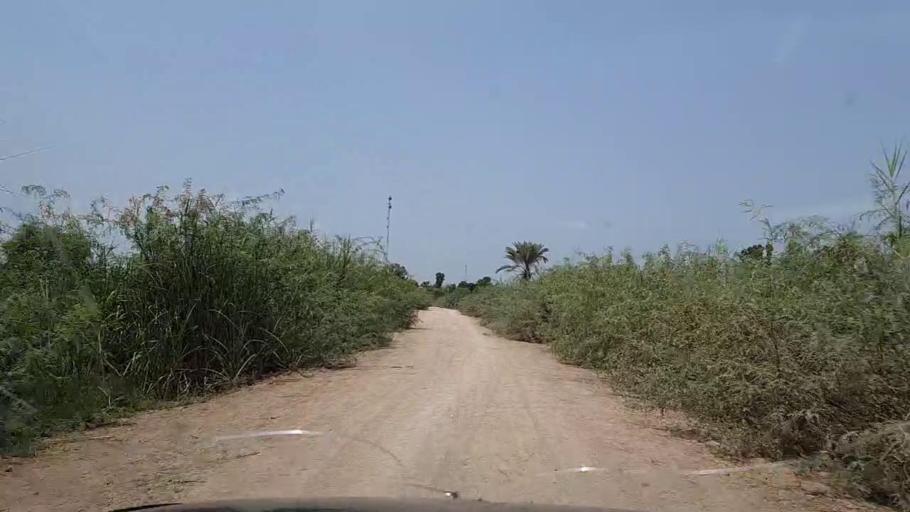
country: PK
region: Sindh
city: Pano Aqil
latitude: 27.9177
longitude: 69.2046
